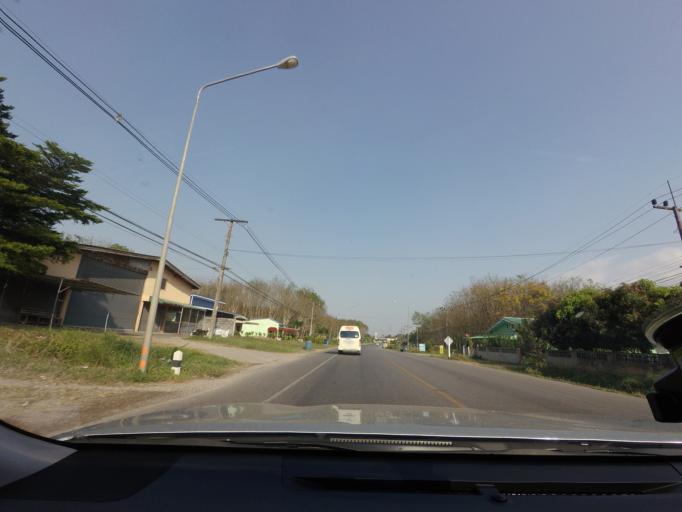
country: TH
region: Surat Thani
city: Phrasaeng
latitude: 8.5734
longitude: 99.2216
